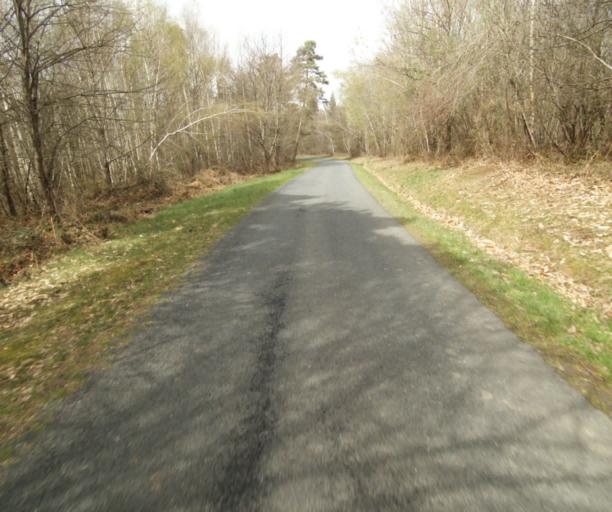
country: FR
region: Limousin
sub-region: Departement de la Correze
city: Argentat
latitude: 45.1980
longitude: 1.9086
